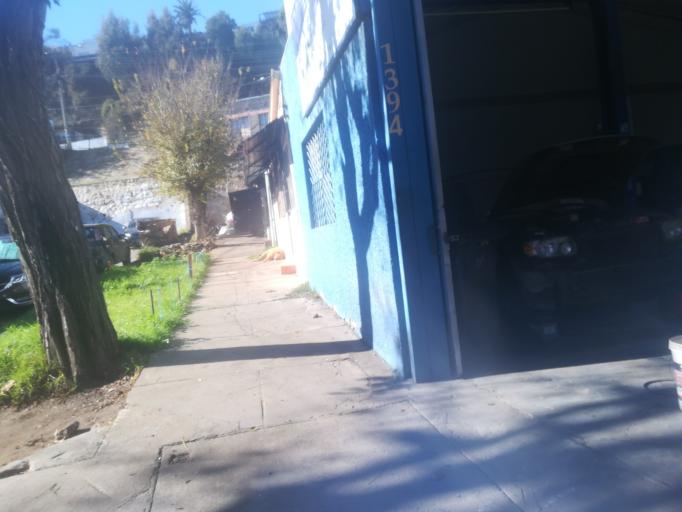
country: CL
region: Valparaiso
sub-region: Provincia de Valparaiso
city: Vina del Mar
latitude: -33.0114
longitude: -71.5409
